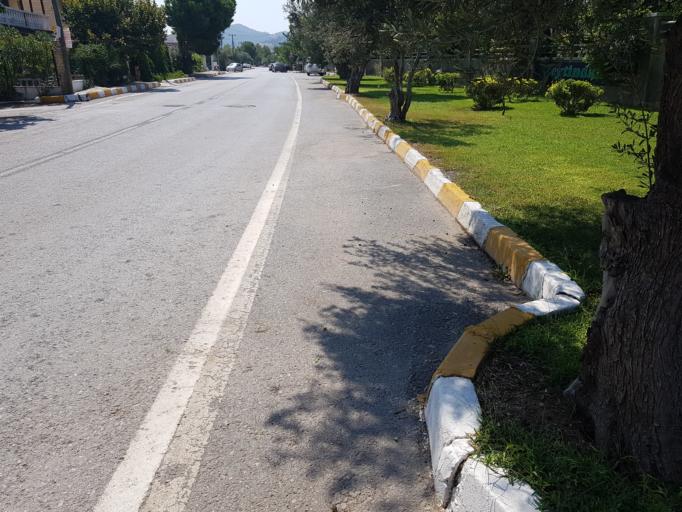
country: TR
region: Izmir
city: Urla
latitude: 38.3938
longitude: 26.7422
